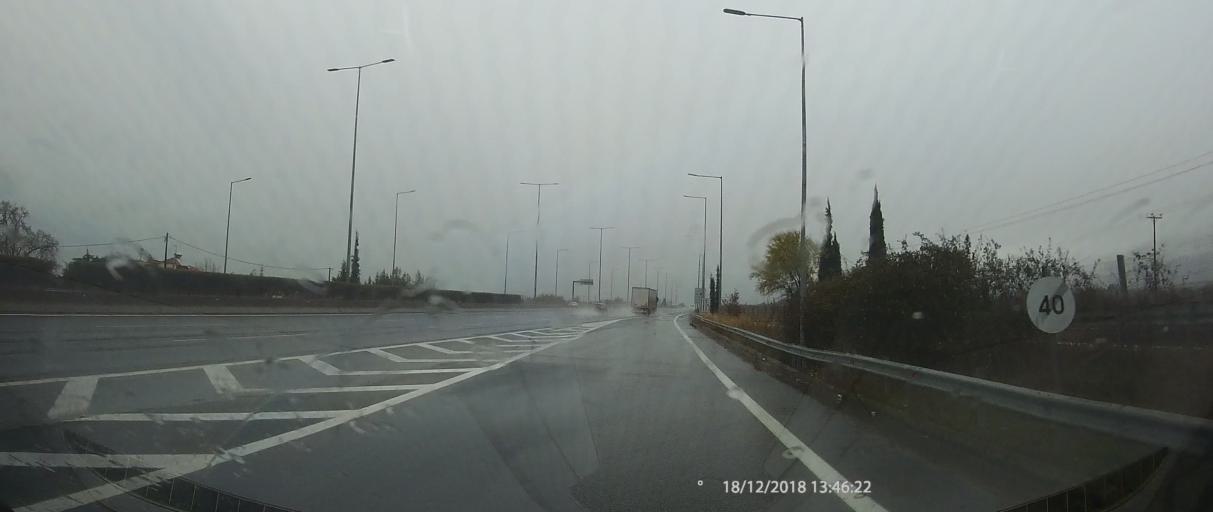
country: GR
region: Central Macedonia
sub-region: Nomos Pierias
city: Leptokarya
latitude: 40.0980
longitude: 22.5551
